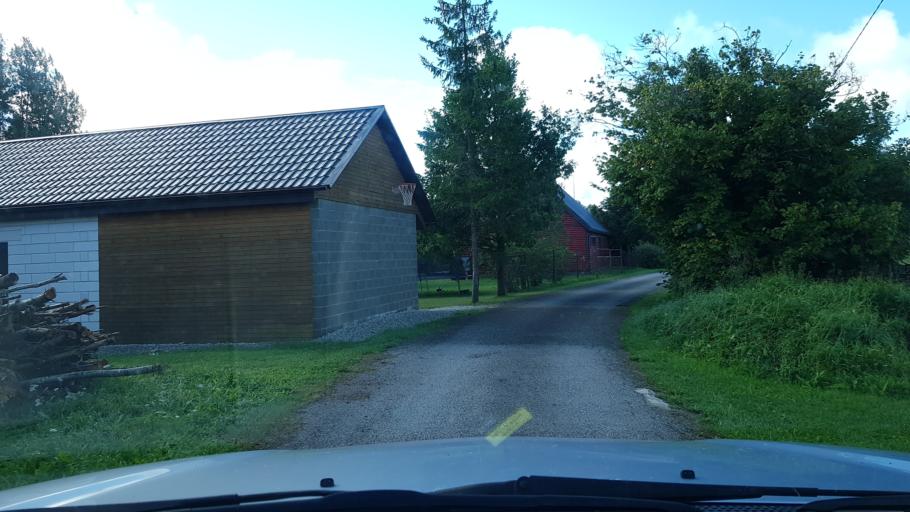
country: EE
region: Harju
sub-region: Rae vald
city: Vaida
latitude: 59.2530
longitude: 25.0271
